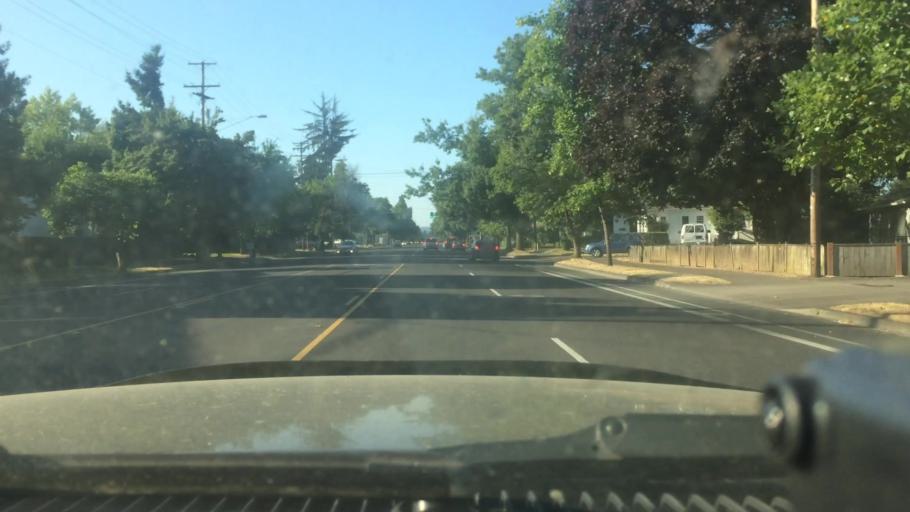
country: US
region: Oregon
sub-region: Lane County
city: Eugene
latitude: 44.0894
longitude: -123.1255
